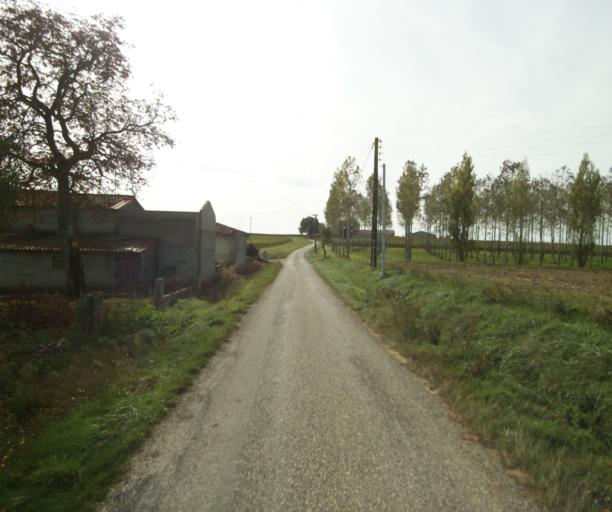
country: FR
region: Midi-Pyrenees
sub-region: Departement du Gers
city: Eauze
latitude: 43.8502
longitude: 0.1398
